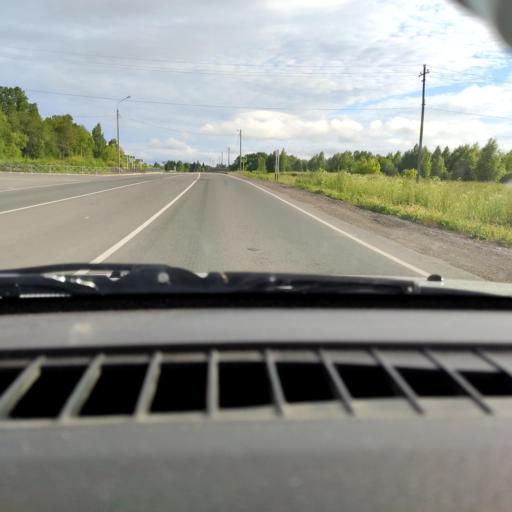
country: RU
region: Perm
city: Kungur
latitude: 57.3484
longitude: 56.9679
